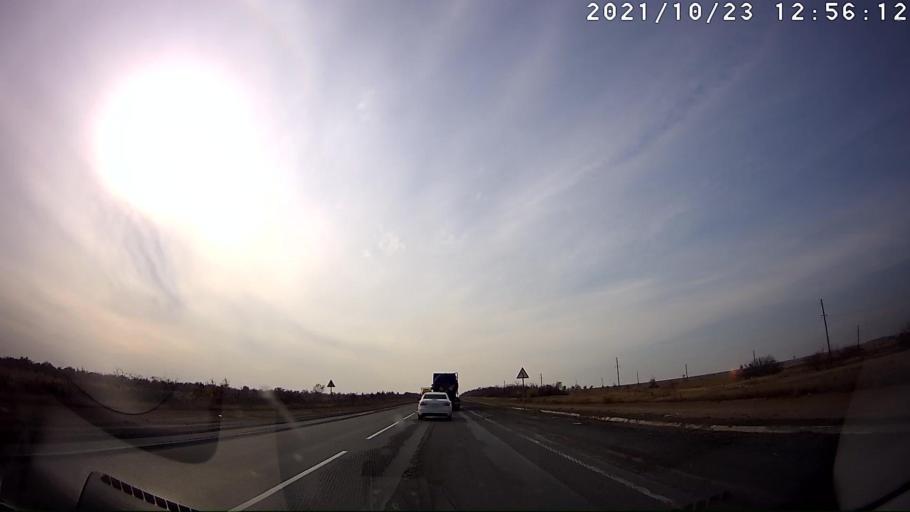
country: RU
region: Volgograd
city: Dubovka
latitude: 49.0480
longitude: 44.7793
